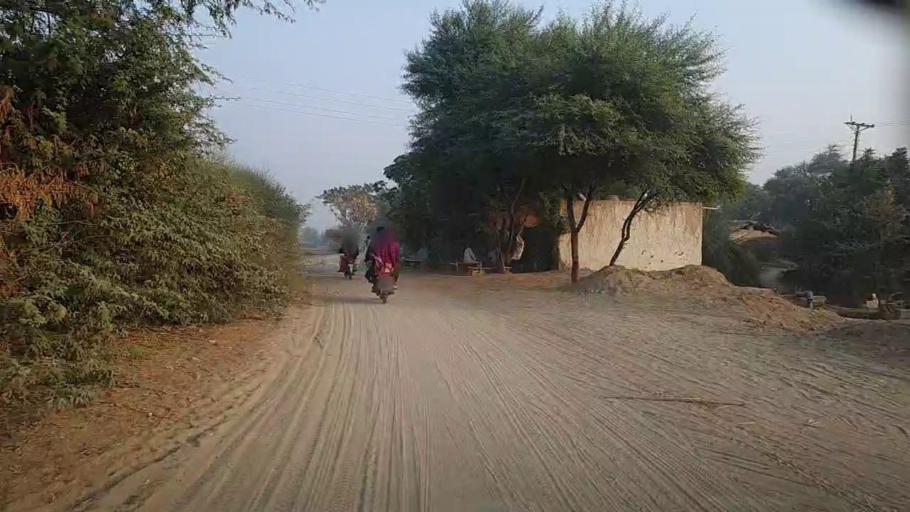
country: PK
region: Sindh
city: Bozdar
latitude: 27.0827
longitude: 68.5671
